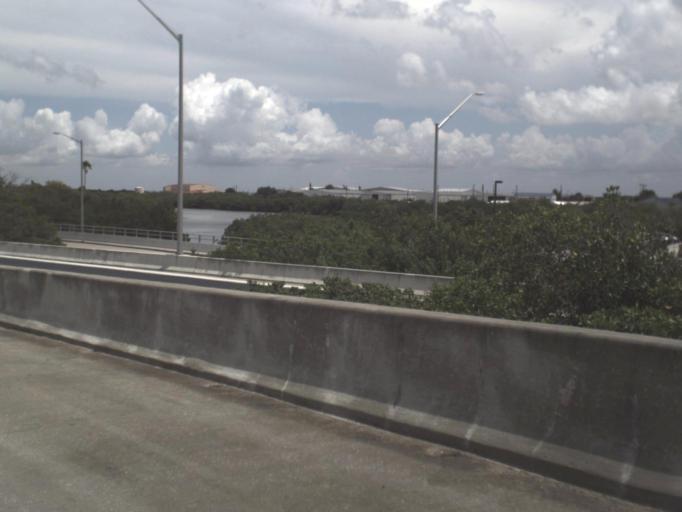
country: US
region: Florida
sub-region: Pinellas County
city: South Highpoint
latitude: 27.9116
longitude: -82.7006
